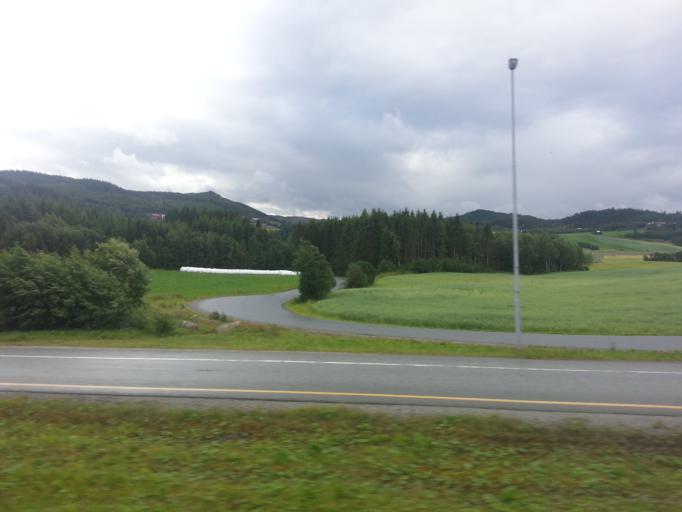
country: NO
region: Sor-Trondelag
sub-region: Malvik
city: Malvik
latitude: 63.4256
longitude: 10.6884
